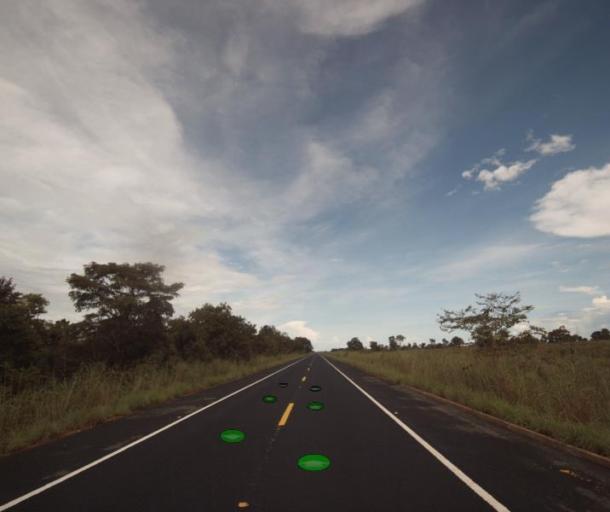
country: BR
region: Goias
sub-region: Sao Miguel Do Araguaia
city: Sao Miguel do Araguaia
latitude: -13.2601
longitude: -50.5186
